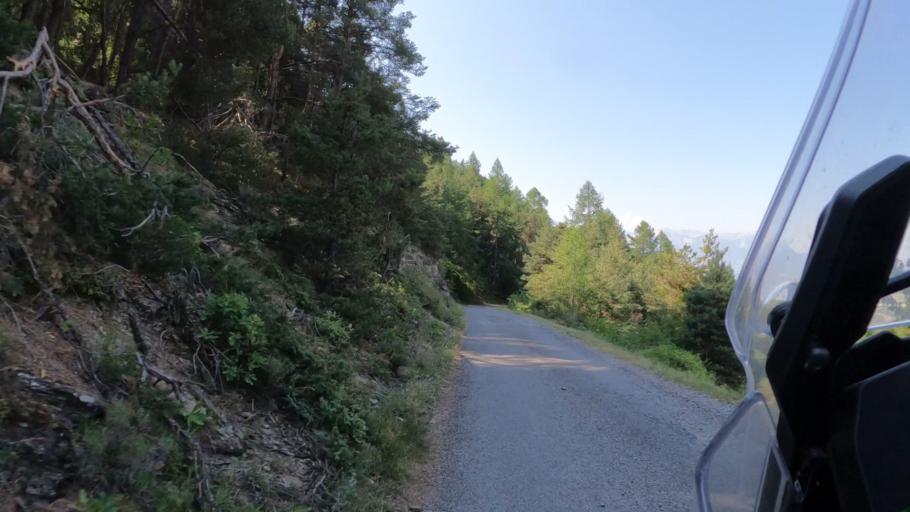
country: FR
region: Provence-Alpes-Cote d'Azur
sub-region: Departement des Hautes-Alpes
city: Embrun
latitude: 44.5916
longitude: 6.5437
